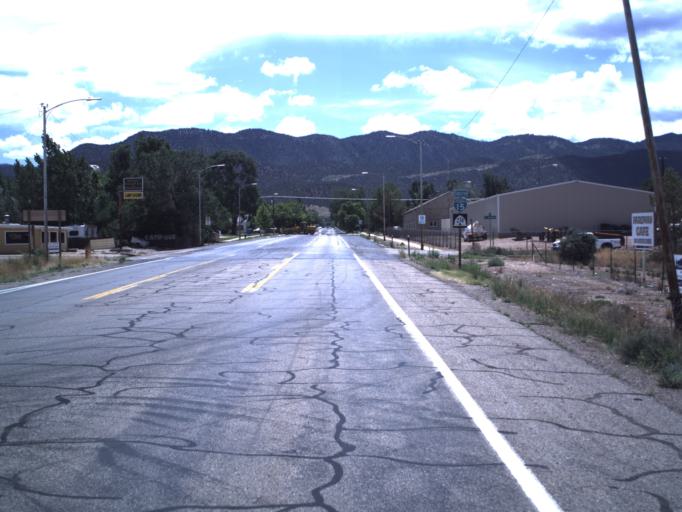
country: US
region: Utah
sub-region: Iron County
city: Parowan
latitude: 37.8511
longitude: -112.8278
